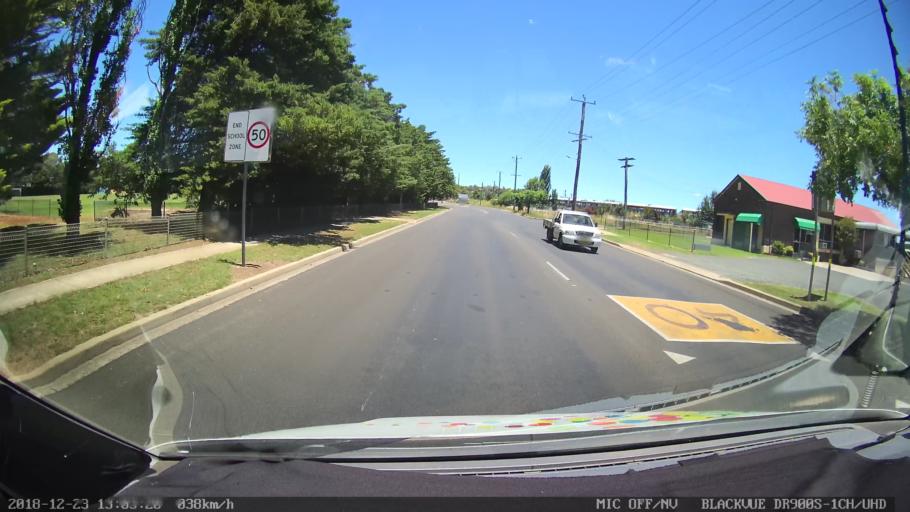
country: AU
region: New South Wales
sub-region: Armidale Dumaresq
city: Armidale
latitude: -30.5110
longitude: 151.6496
